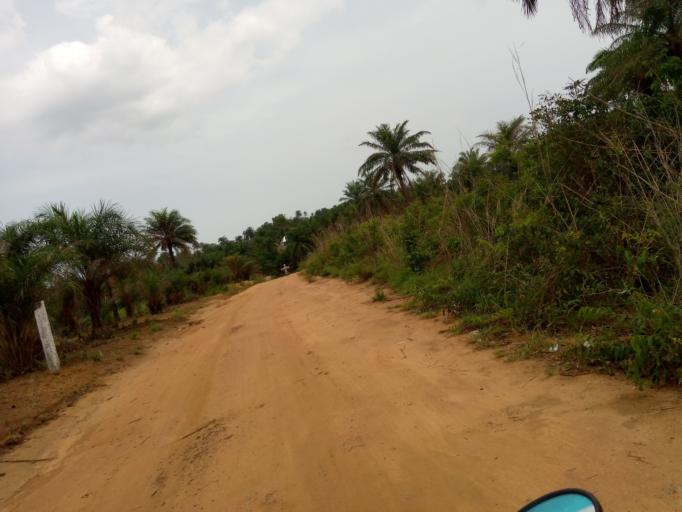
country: SL
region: Western Area
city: Waterloo
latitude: 8.3423
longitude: -13.0149
